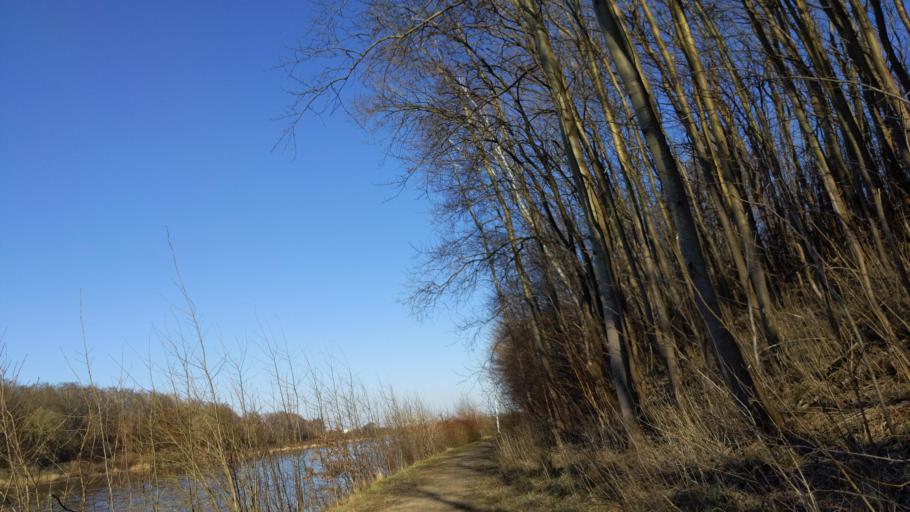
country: DE
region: Schleswig-Holstein
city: Bad Schwartau
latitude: 53.9012
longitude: 10.7054
